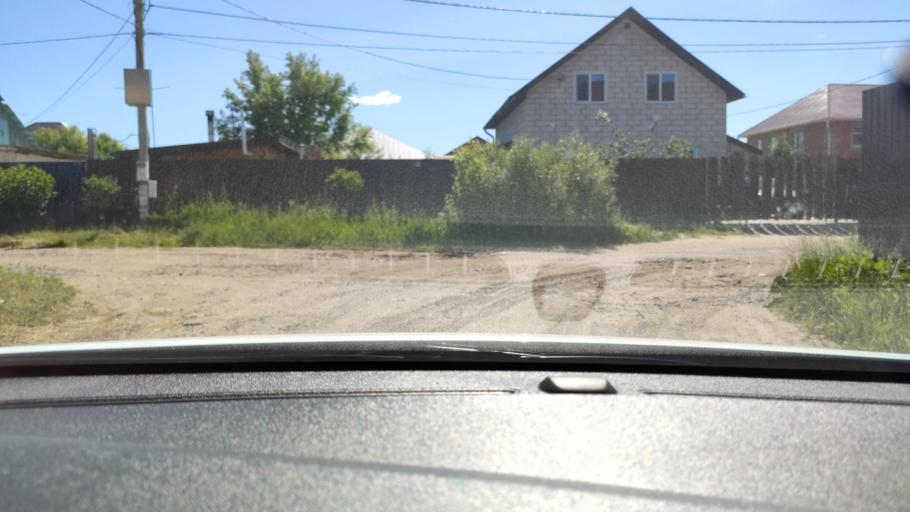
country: RU
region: Tatarstan
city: Stolbishchi
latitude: 55.7477
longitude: 49.2845
